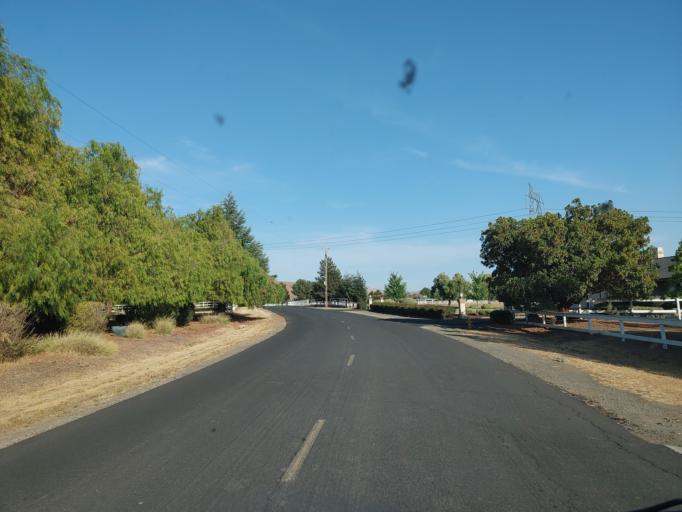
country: US
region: California
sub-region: San Benito County
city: Ridgemark
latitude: 36.8026
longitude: -121.3313
